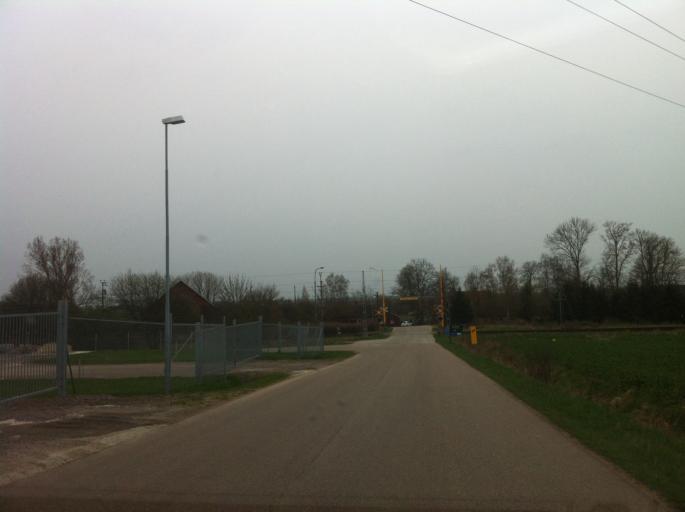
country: SE
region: Skane
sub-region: Svalovs Kommun
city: Kagerod
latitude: 55.9708
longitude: 13.0941
